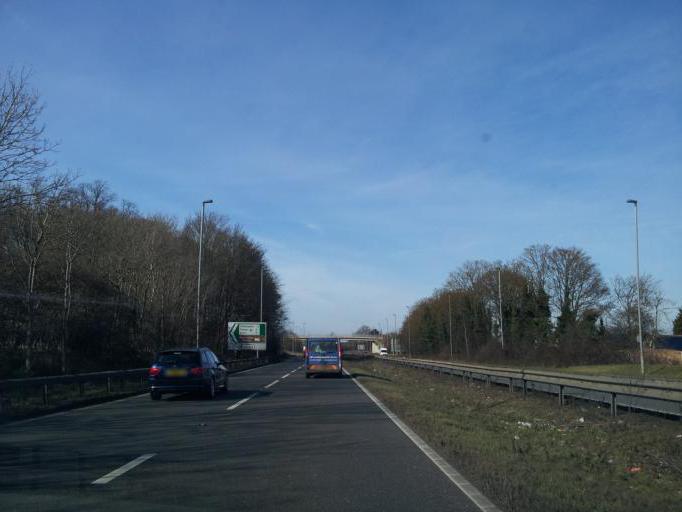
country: GB
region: England
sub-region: Peterborough
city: Wansford
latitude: 52.5704
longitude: -0.3964
